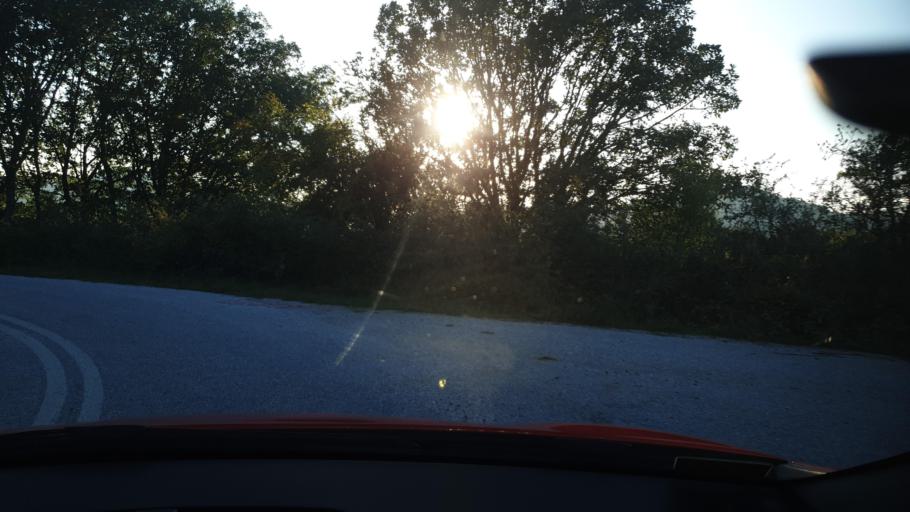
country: GR
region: Central Macedonia
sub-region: Nomos Chalkidikis
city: Galatista
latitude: 40.5108
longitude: 23.2510
